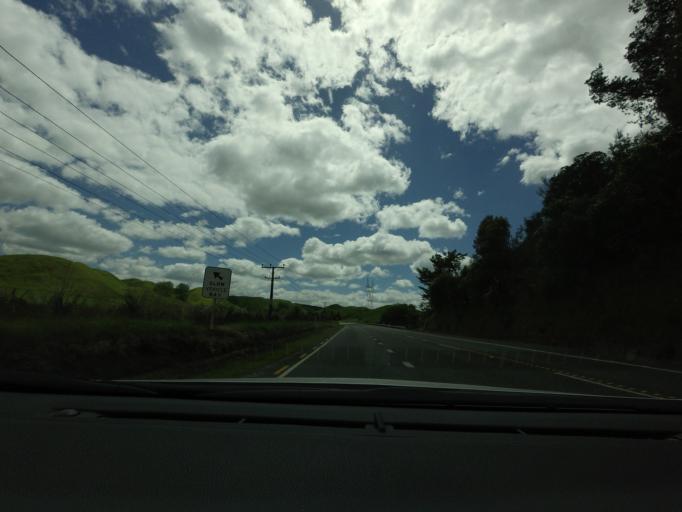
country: NZ
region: Bay of Plenty
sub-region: Rotorua District
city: Rotorua
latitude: -38.3093
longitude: 176.3763
